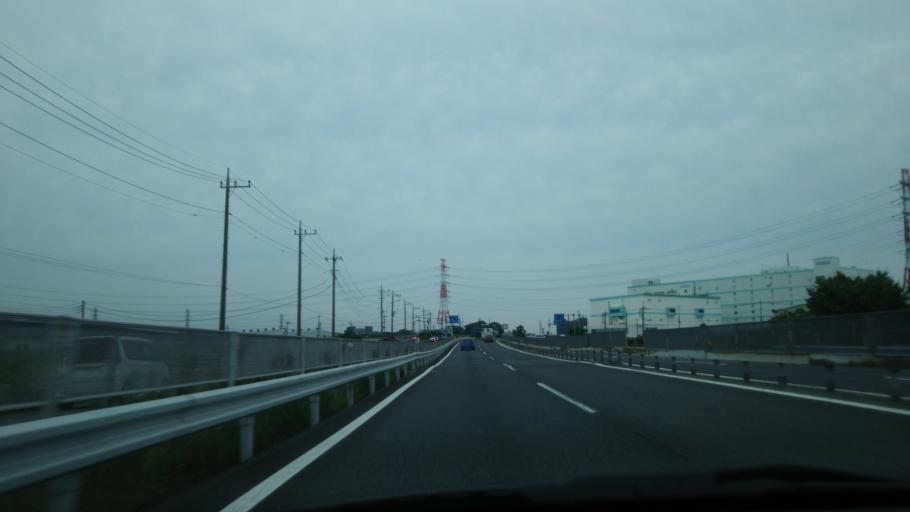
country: JP
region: Kanagawa
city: Isehara
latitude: 35.3996
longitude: 139.3349
